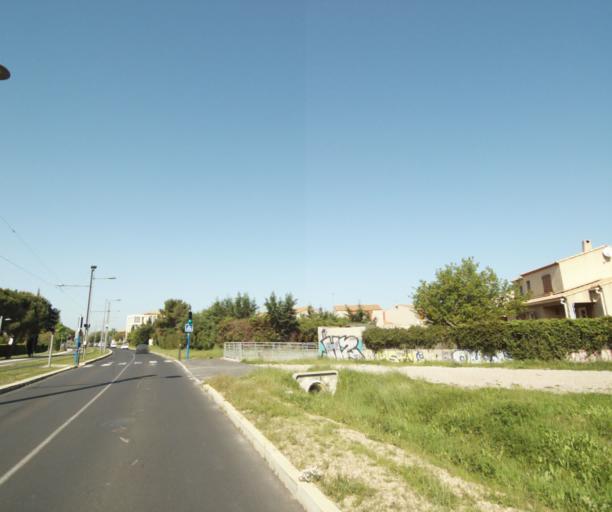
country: FR
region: Languedoc-Roussillon
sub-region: Departement de l'Herault
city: Lattes
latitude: 43.5718
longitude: 3.9098
